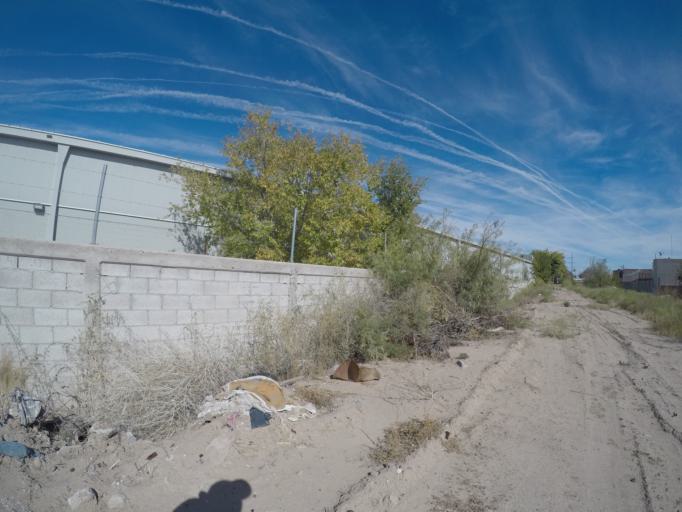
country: MX
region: Chihuahua
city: Ciudad Juarez
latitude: 31.7348
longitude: -106.4426
